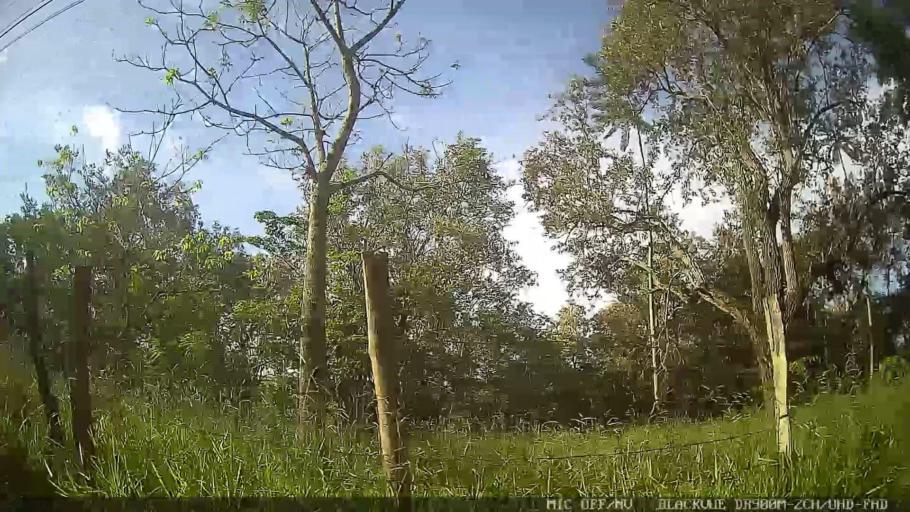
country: BR
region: Sao Paulo
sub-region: Tiete
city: Tiete
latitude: -23.0859
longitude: -47.6915
